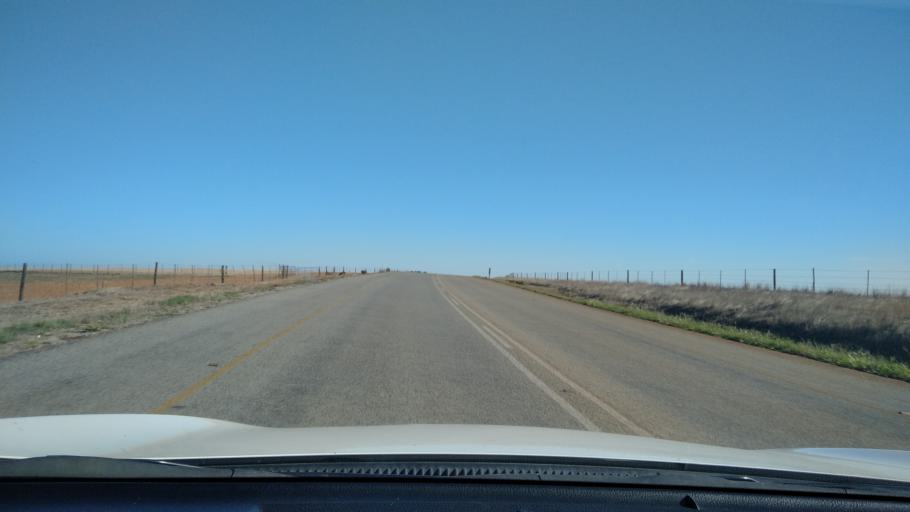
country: ZA
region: Western Cape
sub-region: West Coast District Municipality
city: Malmesbury
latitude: -33.3687
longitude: 18.6512
